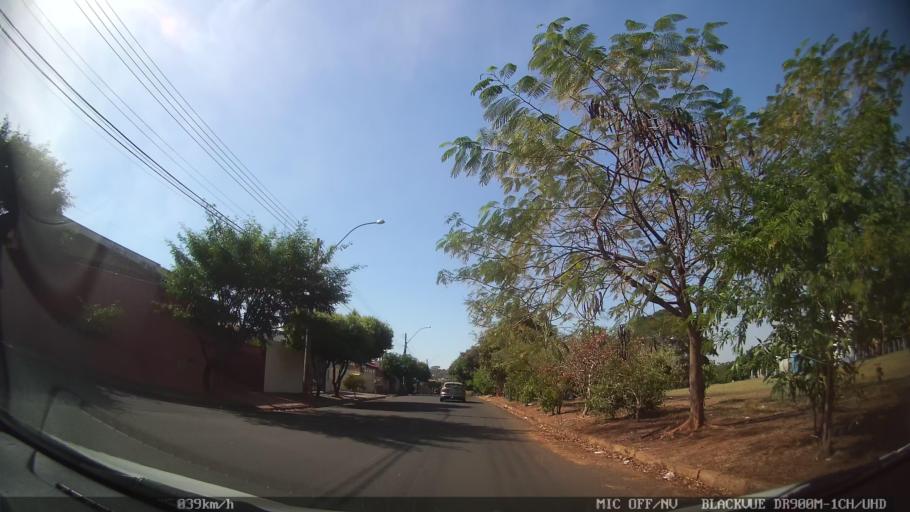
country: BR
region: Sao Paulo
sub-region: Sao Jose Do Rio Preto
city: Sao Jose do Rio Preto
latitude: -20.7886
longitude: -49.4308
